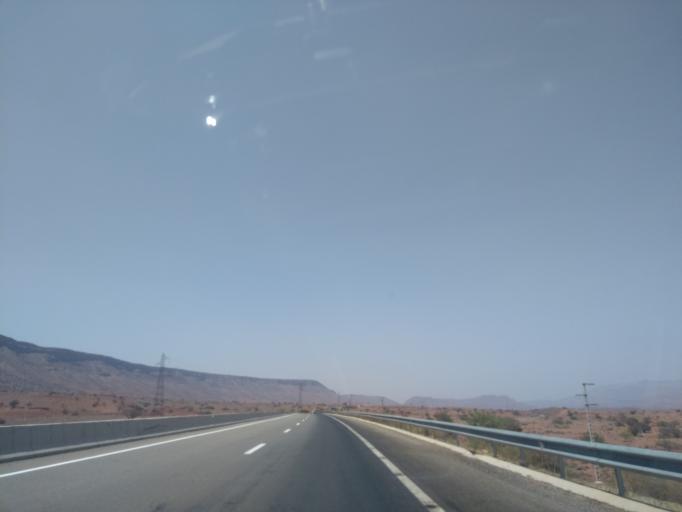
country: MA
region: Marrakech-Tensift-Al Haouz
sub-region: Chichaoua
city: Timezgadiouine
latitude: 30.8829
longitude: -9.0788
